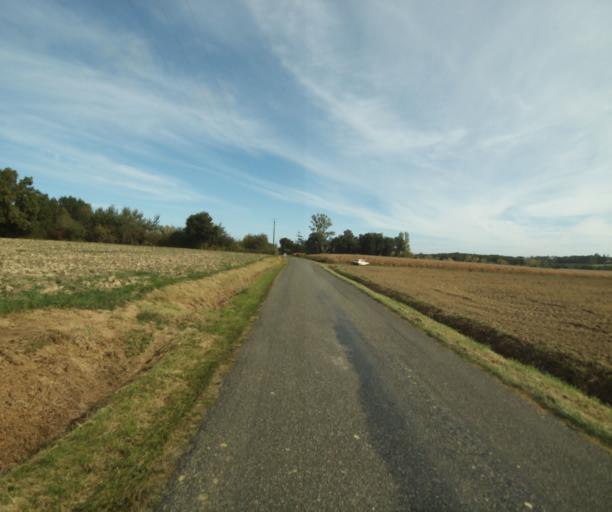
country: FR
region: Midi-Pyrenees
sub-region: Departement du Gers
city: Eauze
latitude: 43.9021
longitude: 0.1380
